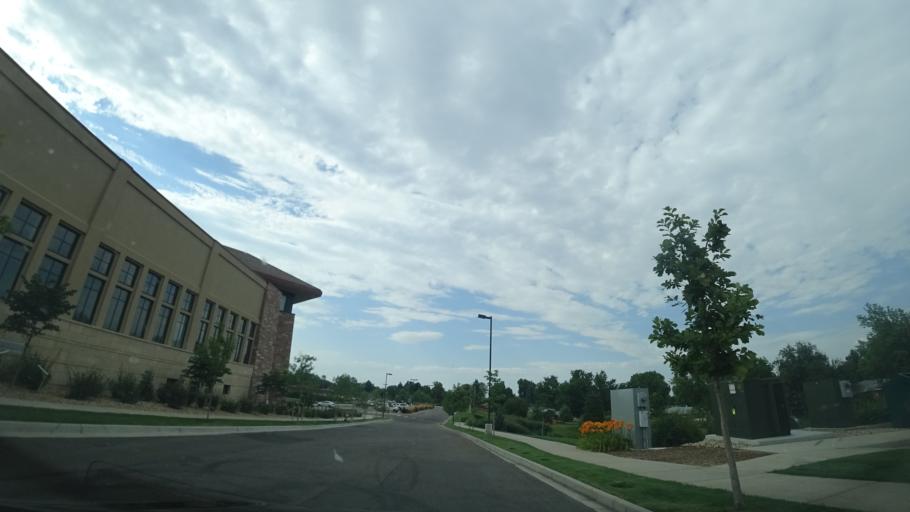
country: US
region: Colorado
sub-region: Jefferson County
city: Lakewood
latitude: 39.7127
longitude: -105.0937
